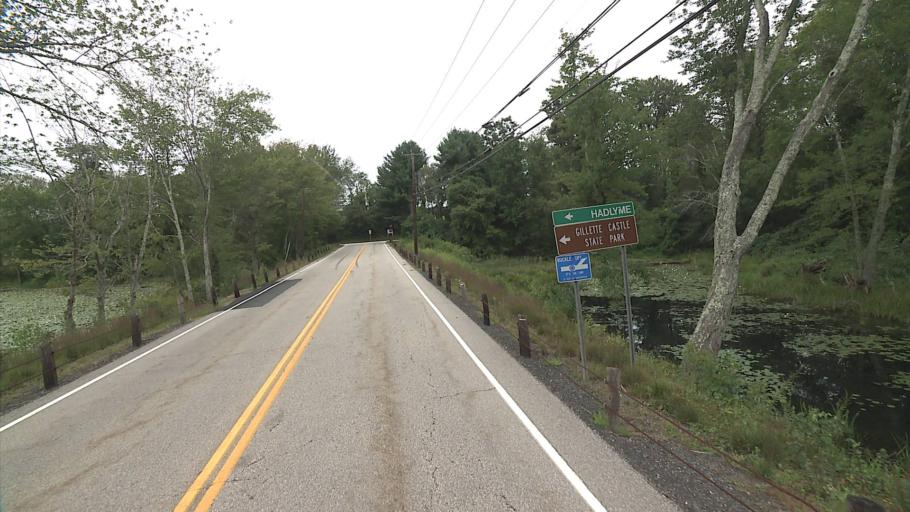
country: US
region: Connecticut
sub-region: Middlesex County
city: Essex Village
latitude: 41.4348
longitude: -72.3397
